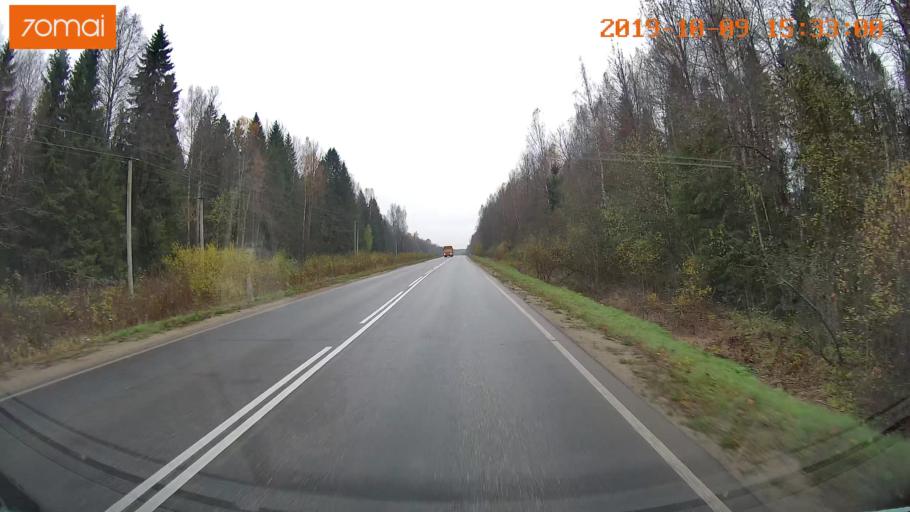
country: RU
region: Kostroma
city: Oktyabr'skiy
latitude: 57.9576
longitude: 41.2682
